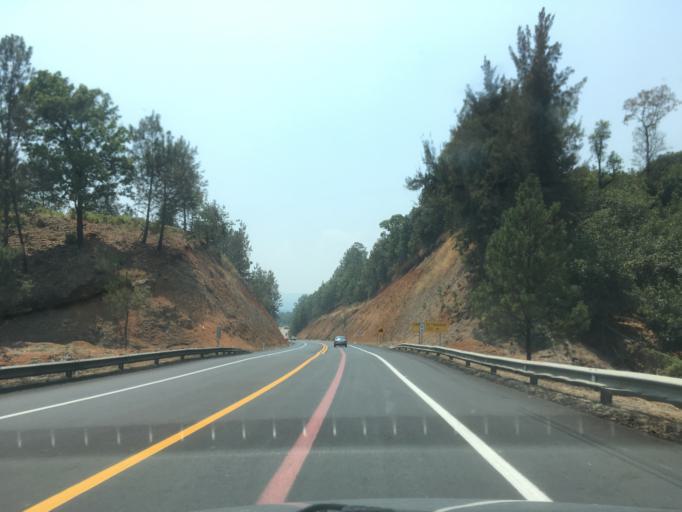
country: MX
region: Michoacan
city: Tingambato
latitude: 19.4454
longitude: -101.8496
